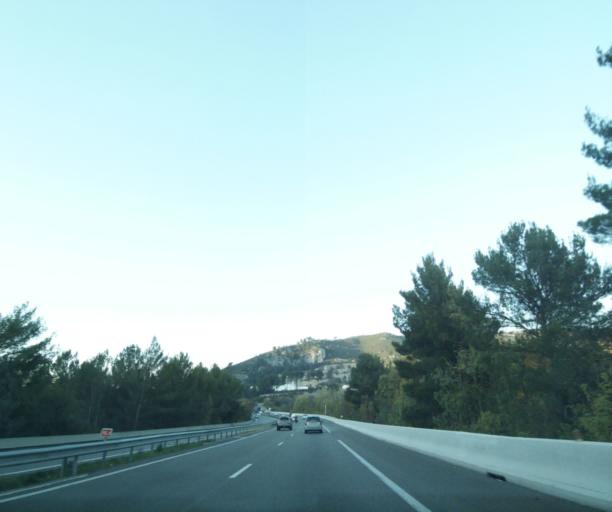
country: FR
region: Provence-Alpes-Cote d'Azur
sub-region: Departement des Bouches-du-Rhone
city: La Destrousse
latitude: 43.3629
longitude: 5.6140
